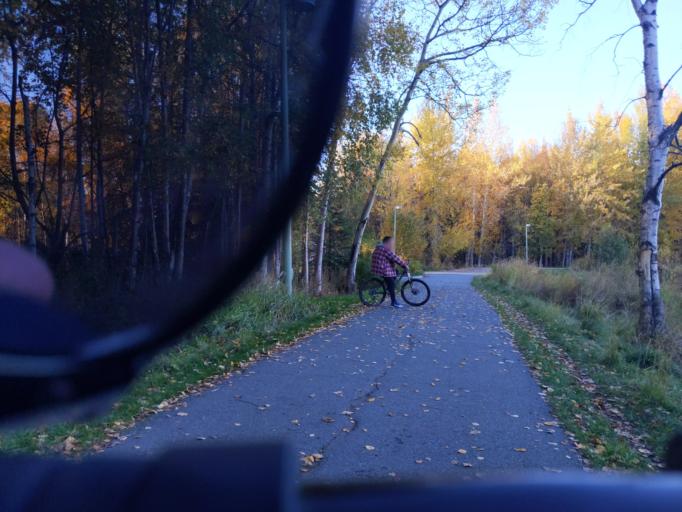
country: US
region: Alaska
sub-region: Anchorage Municipality
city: Anchorage
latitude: 61.1493
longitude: -149.8846
